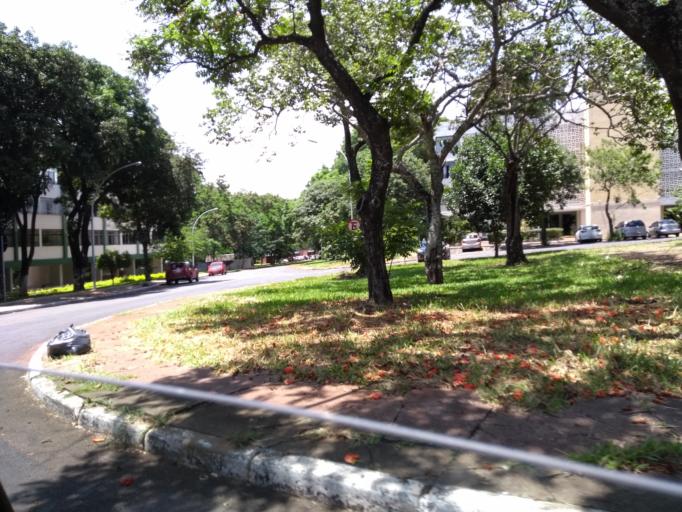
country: BR
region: Federal District
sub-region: Brasilia
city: Brasilia
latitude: -15.8328
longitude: -47.9144
